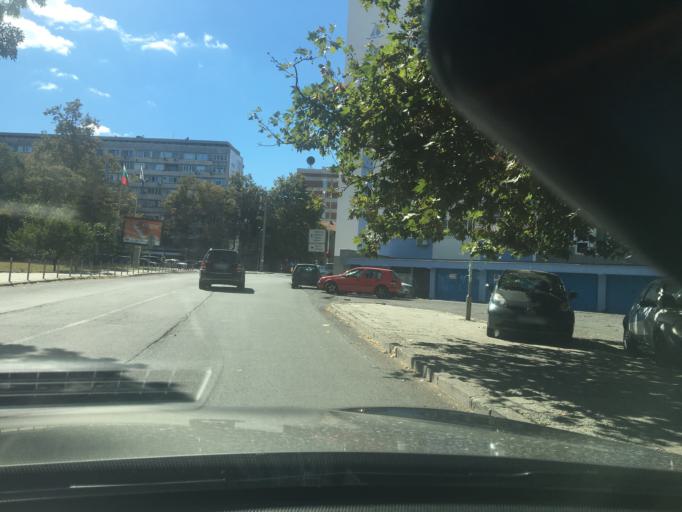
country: BG
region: Burgas
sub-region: Obshtina Burgas
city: Burgas
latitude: 42.5044
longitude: 27.4756
